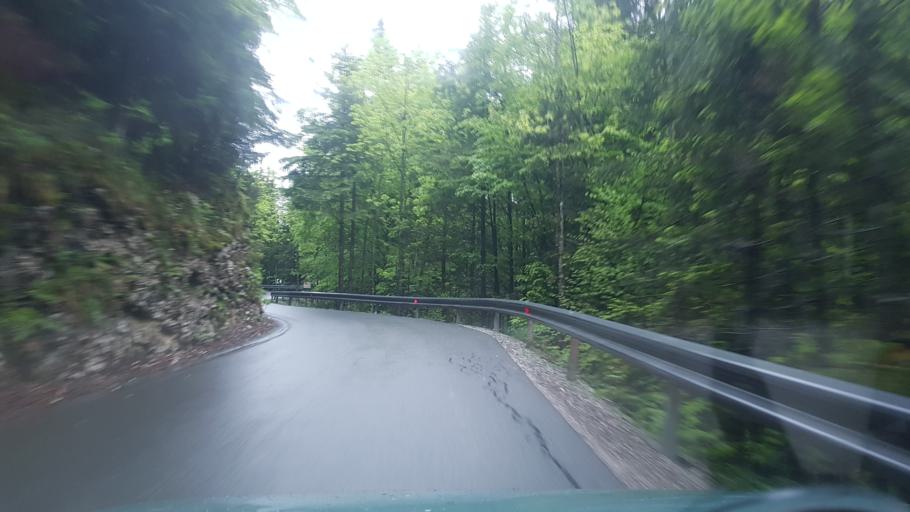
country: SI
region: Bohinj
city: Bohinjska Bistrica
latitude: 46.2711
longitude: 14.0196
